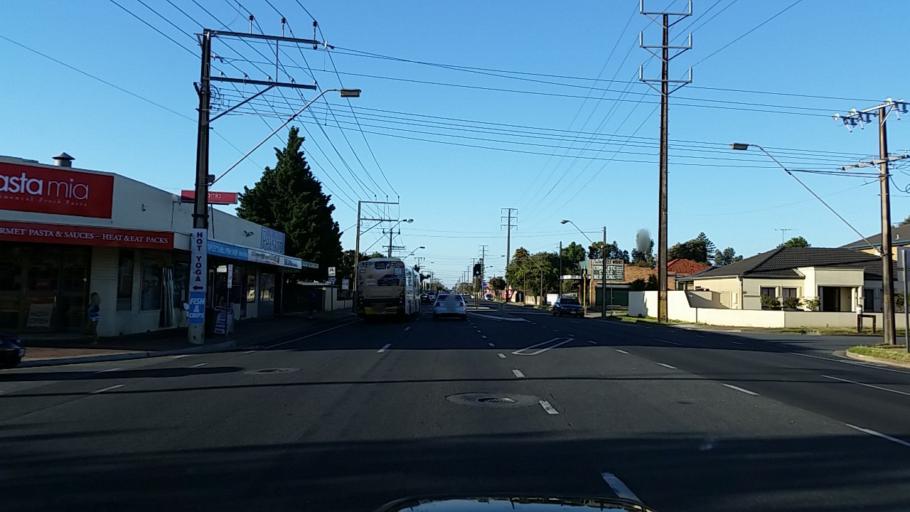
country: AU
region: South Australia
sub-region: Charles Sturt
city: Royal Park
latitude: -34.8858
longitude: 138.5132
